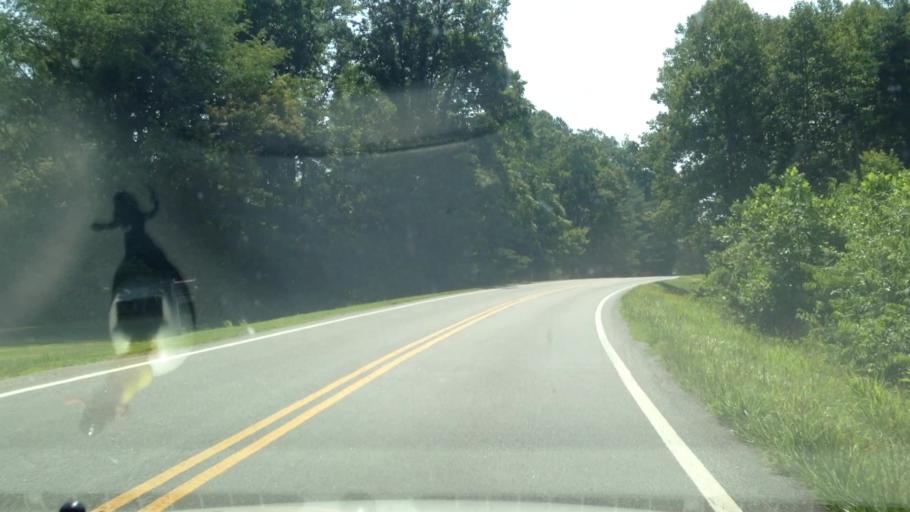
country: US
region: Virginia
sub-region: Patrick County
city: Stuart
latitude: 36.5784
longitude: -80.3642
